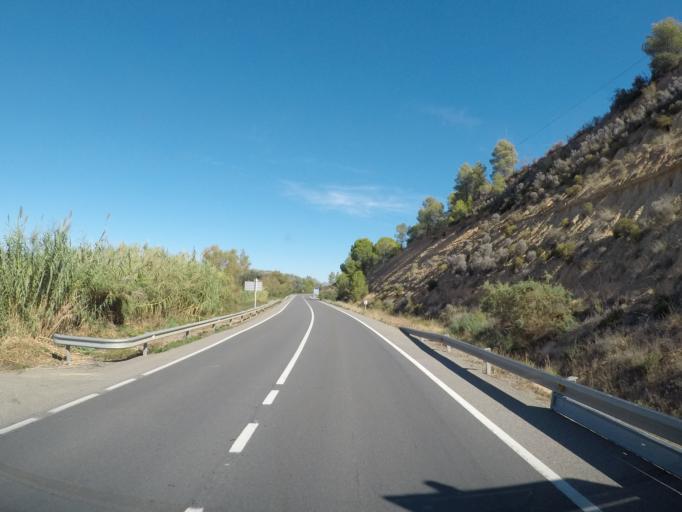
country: ES
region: Catalonia
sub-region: Provincia de Tarragona
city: Ginestar
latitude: 41.0654
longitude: 0.6638
